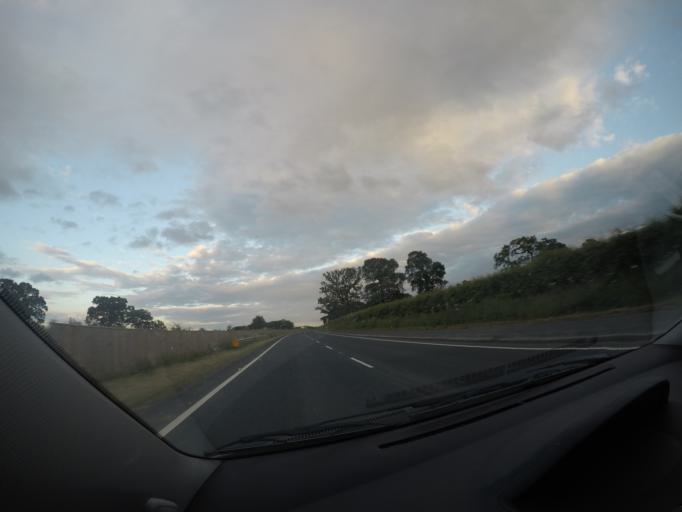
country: GB
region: England
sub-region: North Yorkshire
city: Bedale
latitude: 54.2946
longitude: -1.5545
